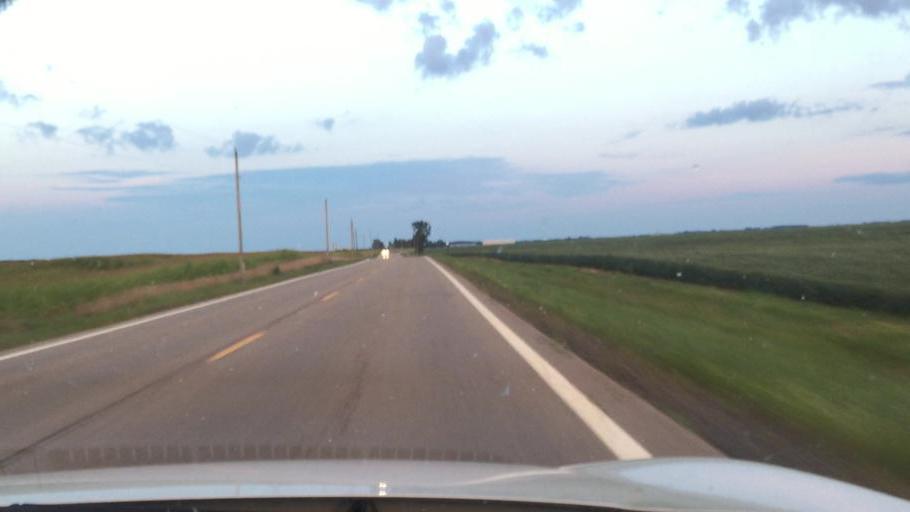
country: US
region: Ohio
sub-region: Madison County
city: Choctaw Lake
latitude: 40.0105
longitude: -83.4522
